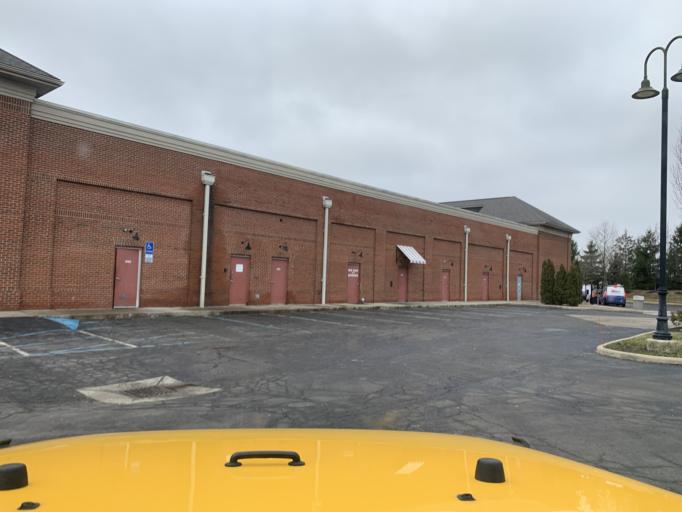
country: US
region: Ohio
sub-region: Franklin County
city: New Albany
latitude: 40.0904
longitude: -82.7958
